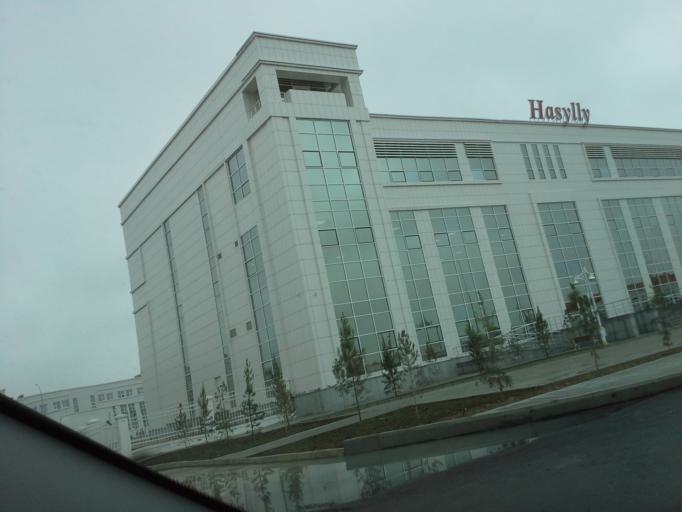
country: TM
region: Ahal
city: Ashgabat
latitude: 37.9514
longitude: 58.4294
